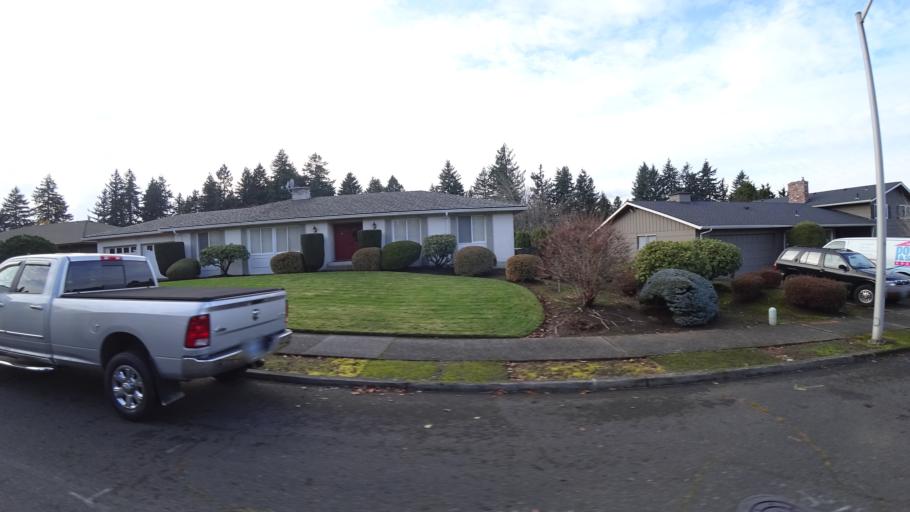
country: US
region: Oregon
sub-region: Multnomah County
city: Lents
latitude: 45.5312
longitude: -122.5230
